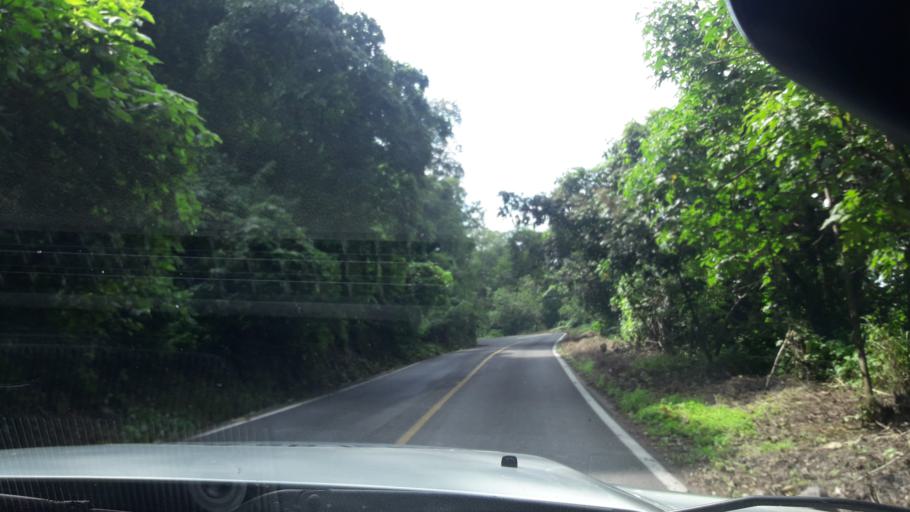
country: MX
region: Colima
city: Suchitlan
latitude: 19.4387
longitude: -103.7095
